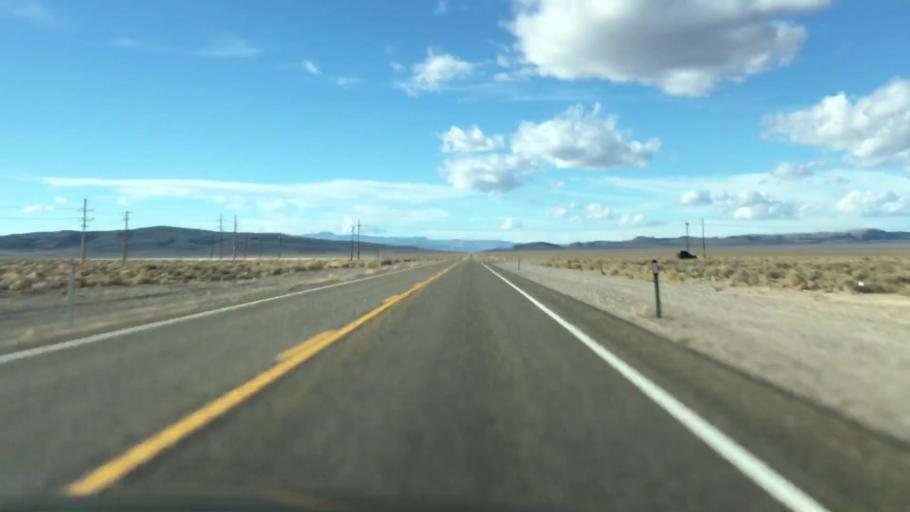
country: US
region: Nevada
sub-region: Nye County
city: Beatty
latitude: 37.1370
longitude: -116.8532
